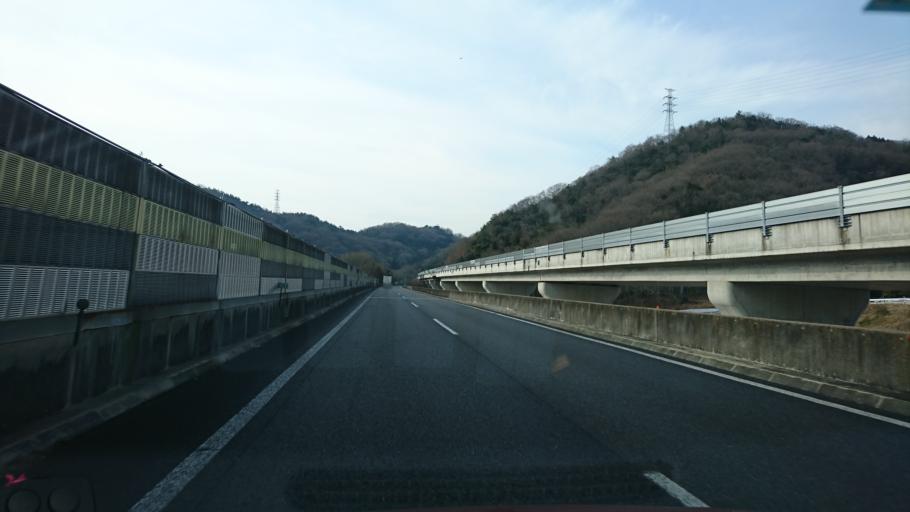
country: JP
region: Okayama
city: Okayama-shi
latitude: 34.7620
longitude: 134.0583
